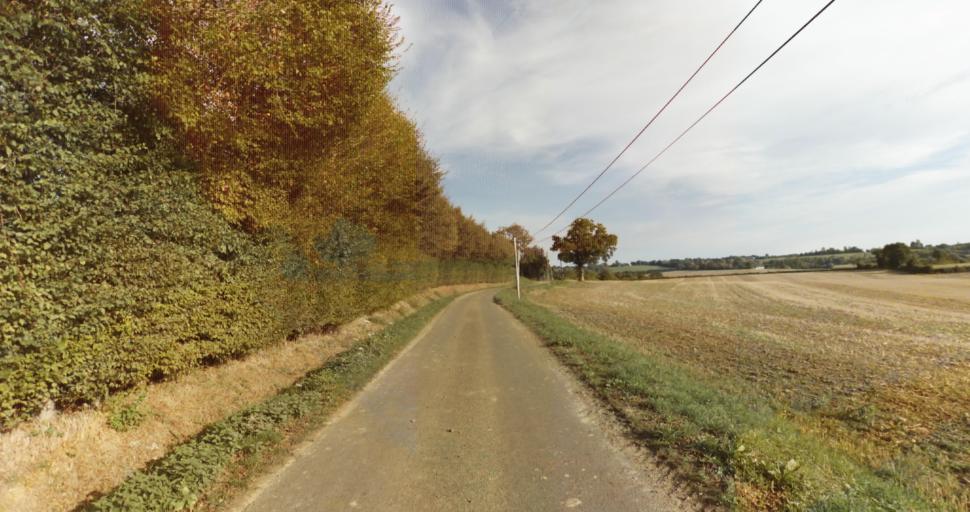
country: FR
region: Lower Normandy
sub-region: Departement de l'Orne
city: Gace
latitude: 48.7130
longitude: 0.3148
